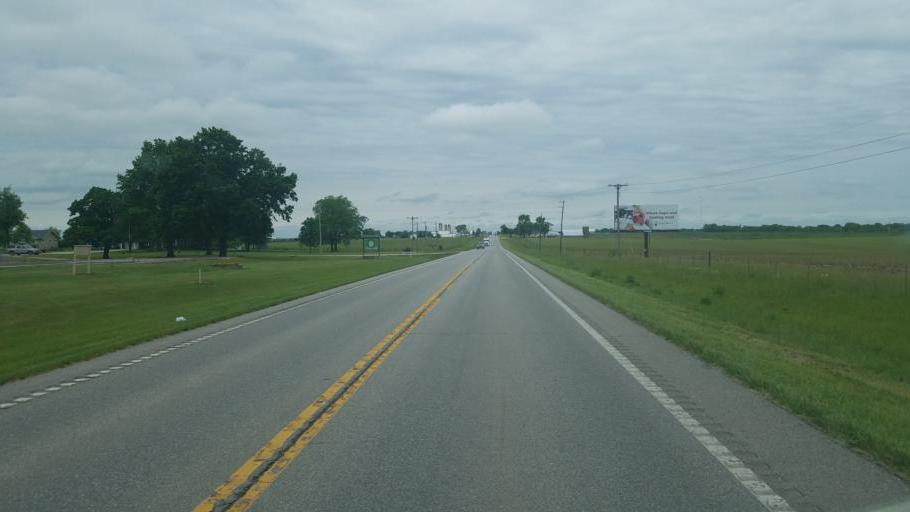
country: US
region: Missouri
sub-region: Morgan County
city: Versailles
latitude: 38.4700
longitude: -92.8088
